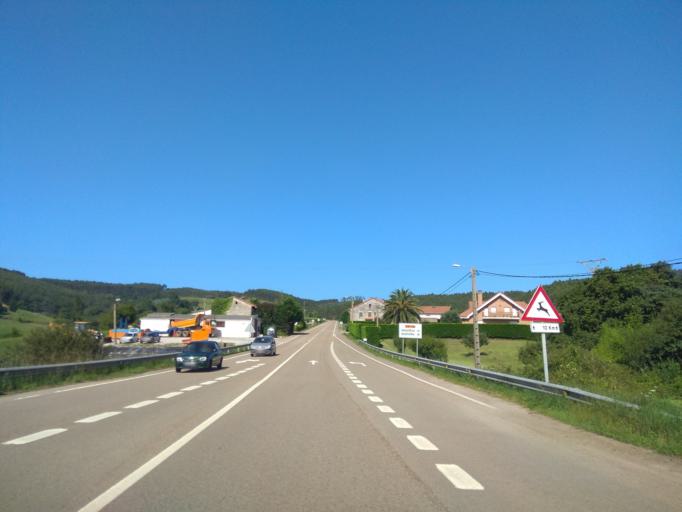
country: ES
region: Cantabria
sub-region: Provincia de Cantabria
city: Bareyo
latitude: 43.4684
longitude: -3.6615
